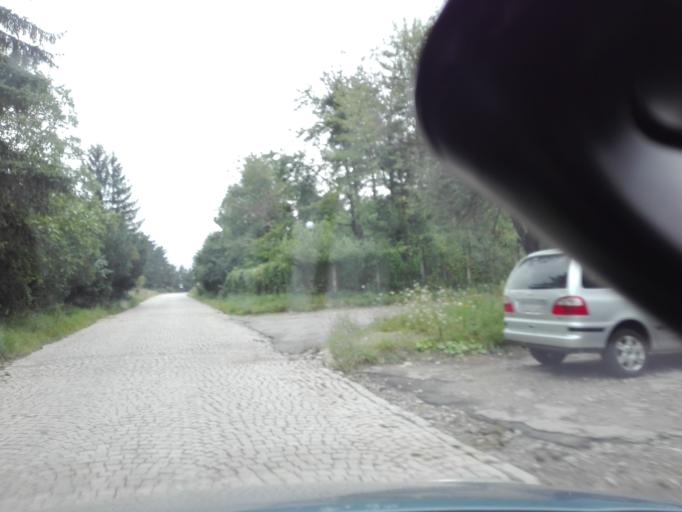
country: BG
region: Sofia-Capital
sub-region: Stolichna Obshtina
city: Sofia
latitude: 42.6049
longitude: 23.3982
